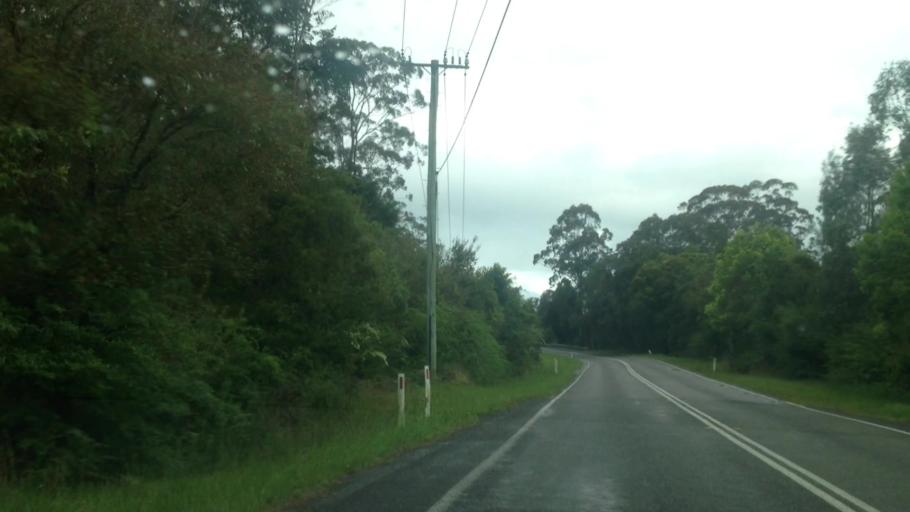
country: AU
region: New South Wales
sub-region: Wyong Shire
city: Little Jilliby
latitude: -33.2580
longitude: 151.3895
